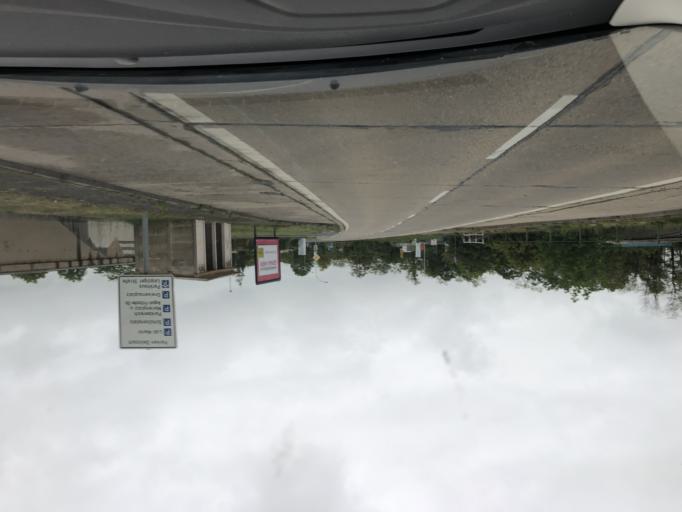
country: DE
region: Saxony
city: Delitzsch
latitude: 51.5384
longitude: 12.3351
